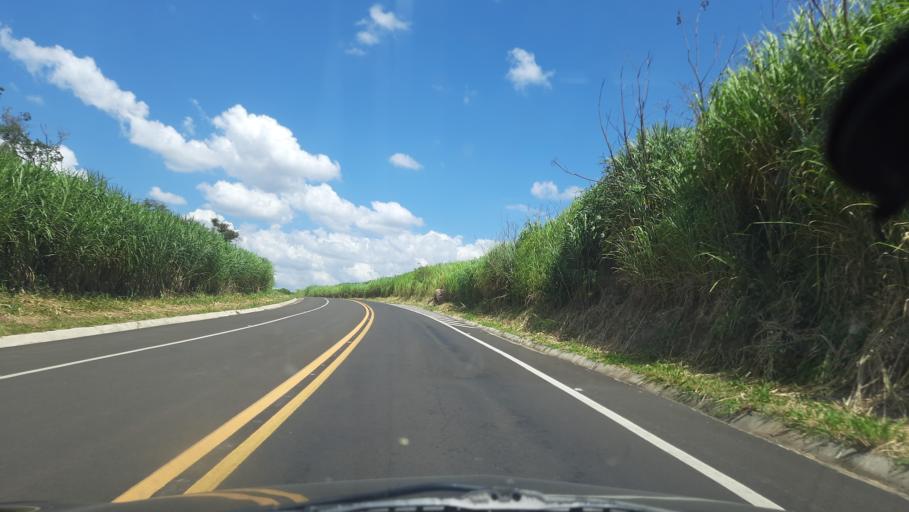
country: BR
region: Sao Paulo
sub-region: Sao Jose Do Rio Pardo
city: Sao Jose do Rio Pardo
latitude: -21.5921
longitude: -46.9933
